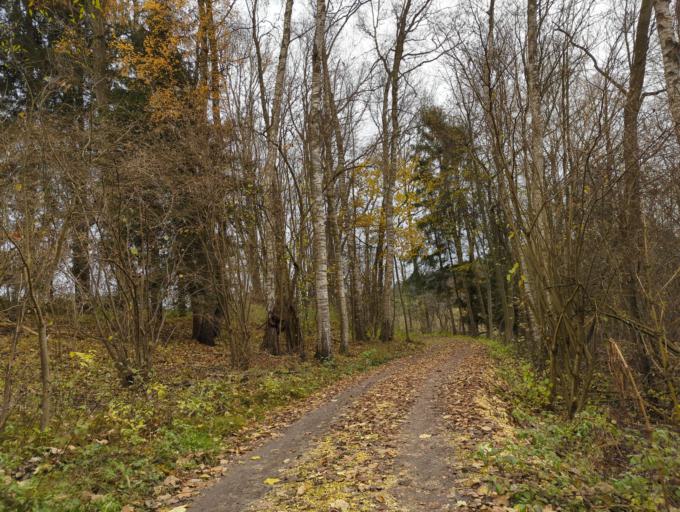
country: DE
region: Bavaria
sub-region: Swabia
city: Guenzburg
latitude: 48.4384
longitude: 10.3115
